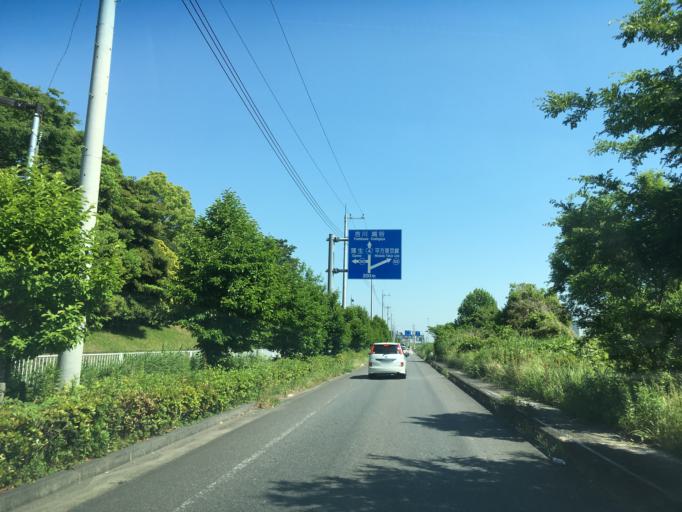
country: JP
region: Saitama
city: Yoshikawa
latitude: 35.8622
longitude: 139.8293
